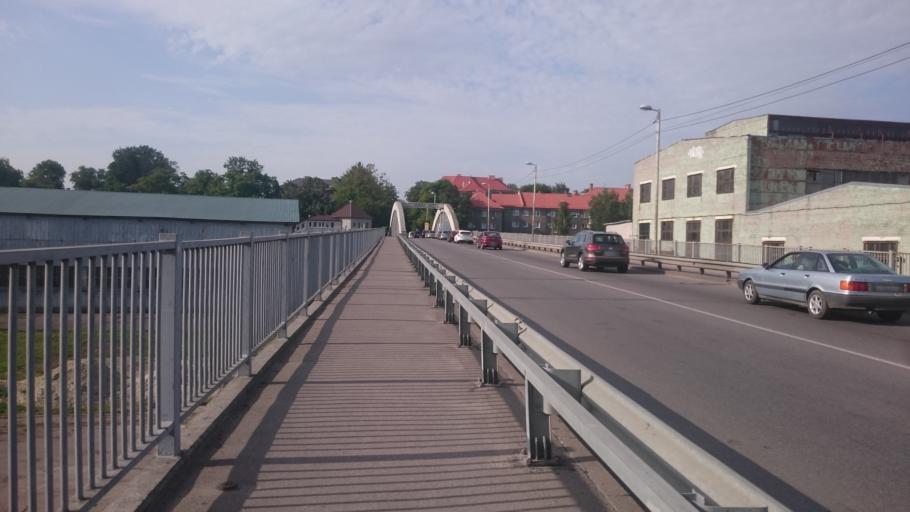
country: RU
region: Kaliningrad
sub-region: Gorod Kaliningrad
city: Kaliningrad
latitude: 54.7096
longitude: 20.4586
